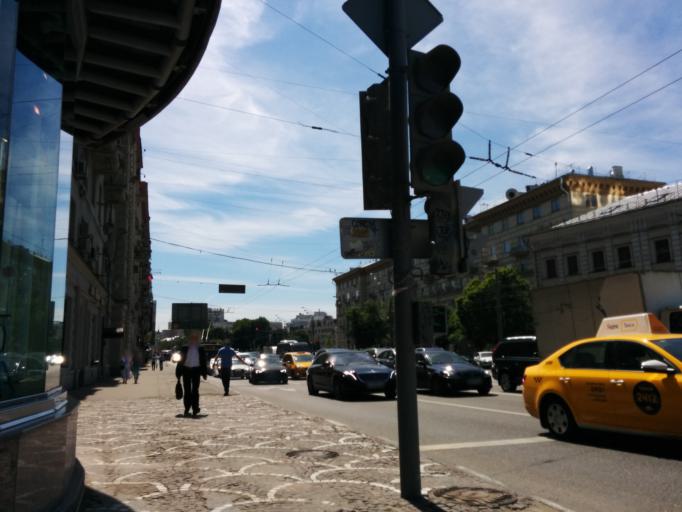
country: RU
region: Moscow
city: Moscow
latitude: 55.7422
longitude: 37.6162
